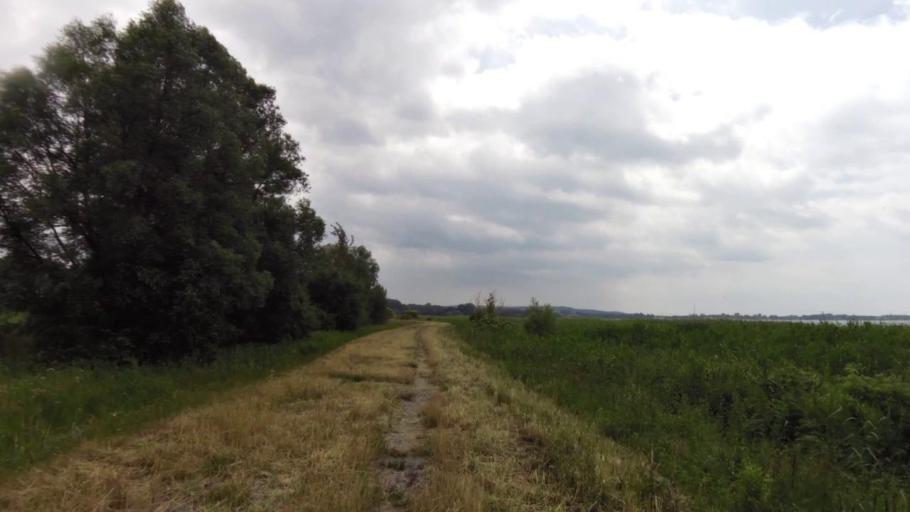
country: PL
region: West Pomeranian Voivodeship
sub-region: Szczecin
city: Szczecin
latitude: 53.4121
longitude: 14.6629
